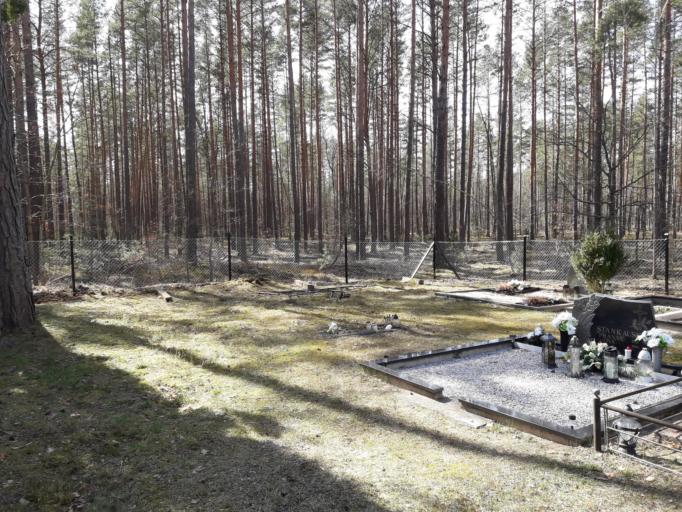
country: LT
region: Alytaus apskritis
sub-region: Alytaus rajonas
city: Daugai
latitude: 54.1958
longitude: 24.3828
